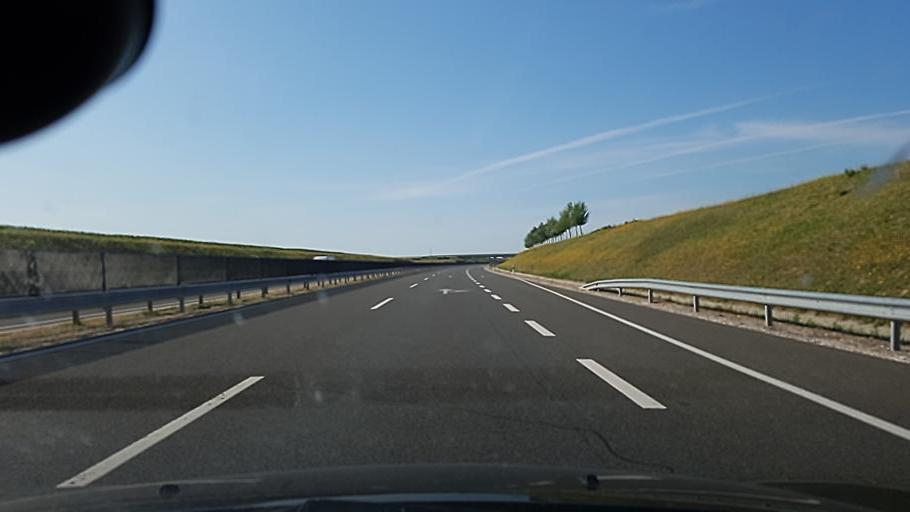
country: HU
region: Tolna
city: Dunafoldvar
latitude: 46.7308
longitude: 18.8747
